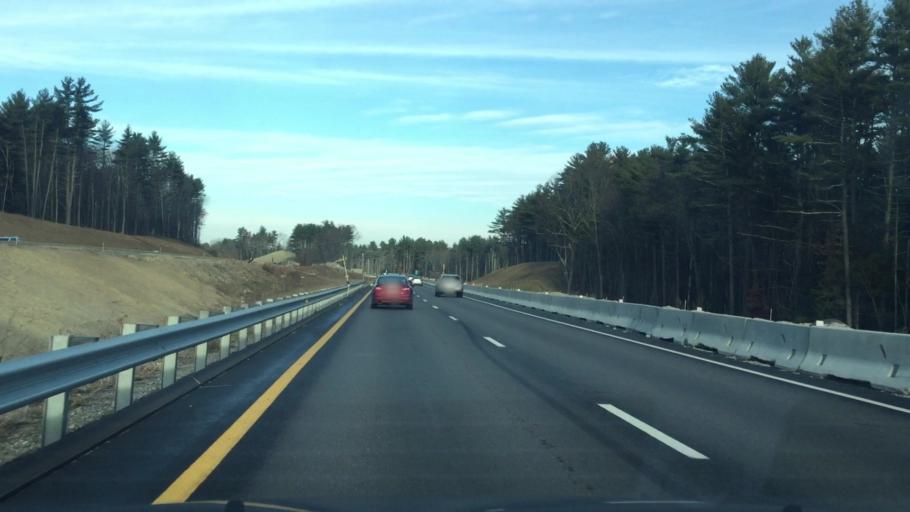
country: US
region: New Hampshire
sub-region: Rockingham County
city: Londonderry
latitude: 42.9371
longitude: -71.3834
